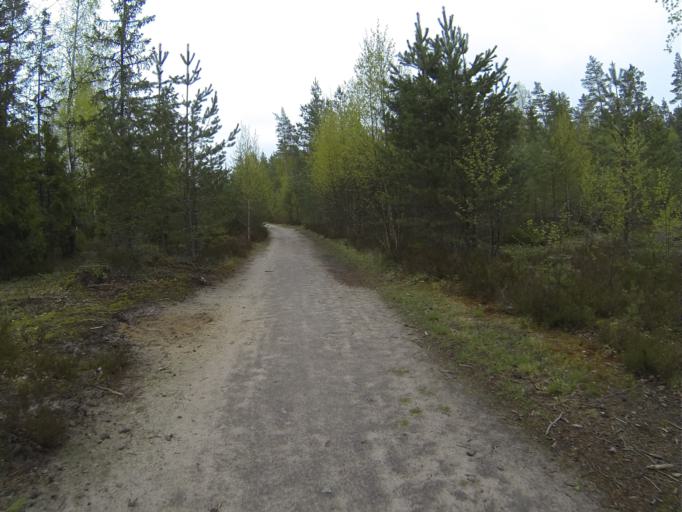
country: FI
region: Varsinais-Suomi
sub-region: Salo
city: Salo
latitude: 60.3981
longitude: 23.1965
